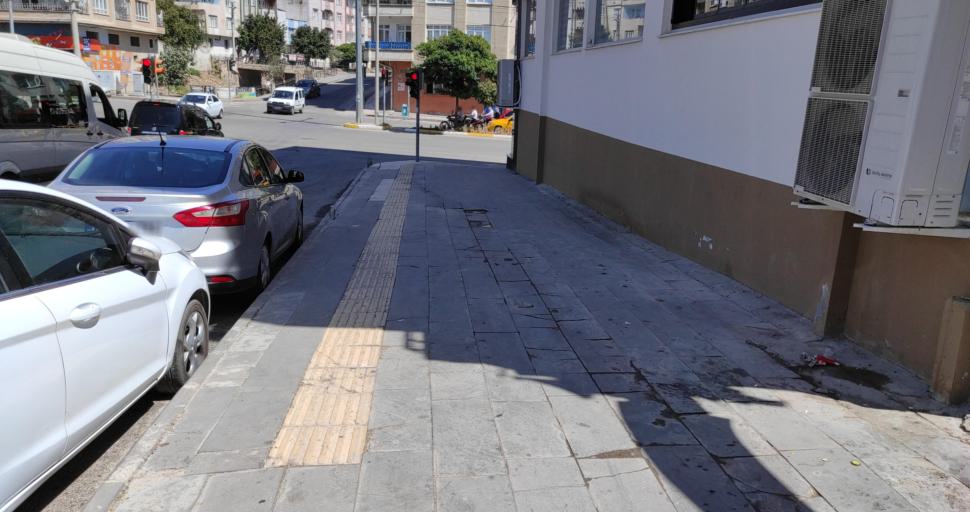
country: TR
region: Kilis
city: Kilis
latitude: 36.7241
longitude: 37.1040
